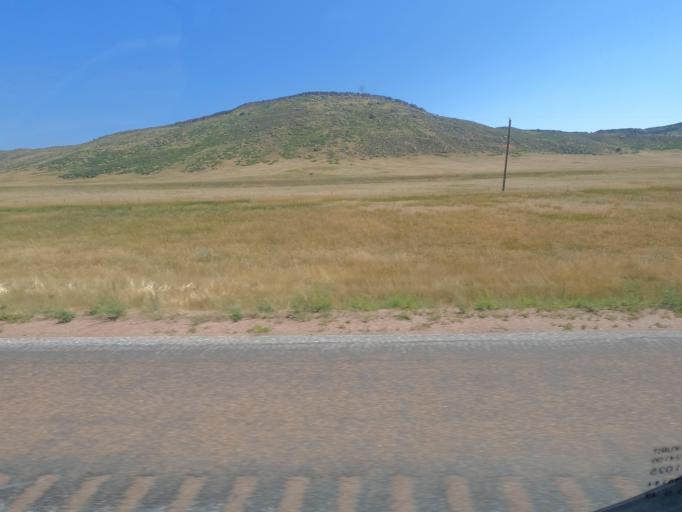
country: US
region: Colorado
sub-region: Larimer County
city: Laporte
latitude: 40.7396
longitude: -105.1700
